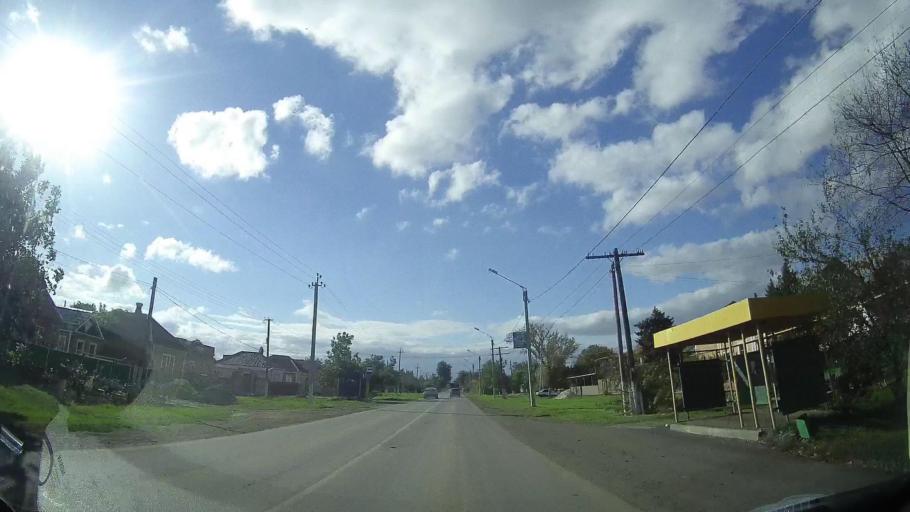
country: RU
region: Rostov
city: Tselina
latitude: 46.5377
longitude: 41.0404
